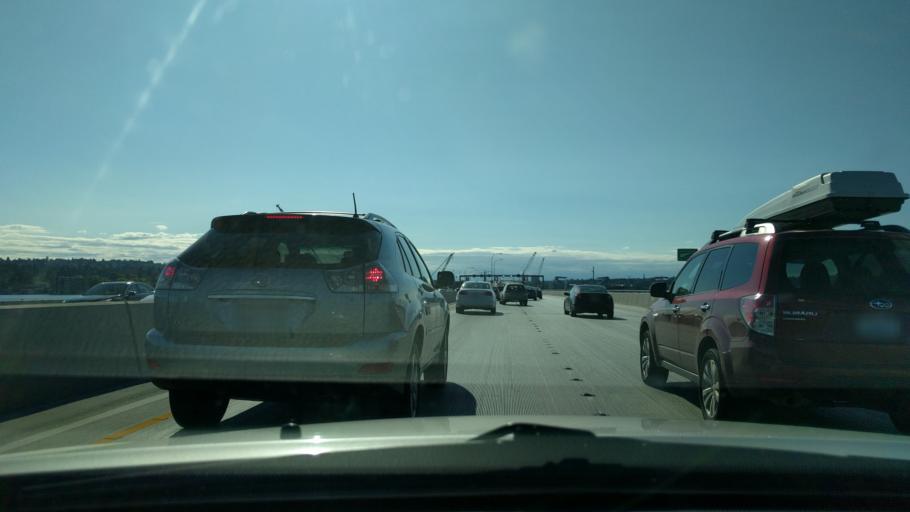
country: US
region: Washington
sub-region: King County
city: Medina
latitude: 47.6415
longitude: -122.2636
